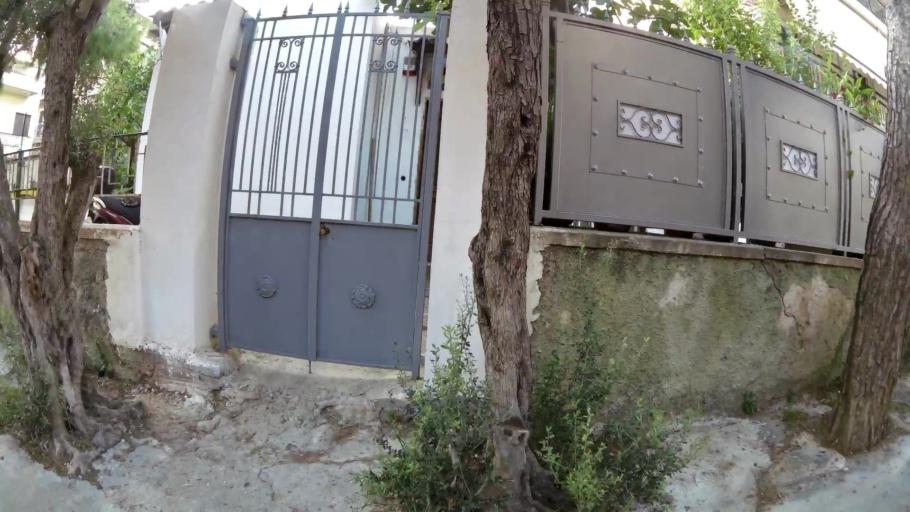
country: GR
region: Attica
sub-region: Nomarchia Athinas
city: Dhafni
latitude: 37.9449
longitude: 23.7320
